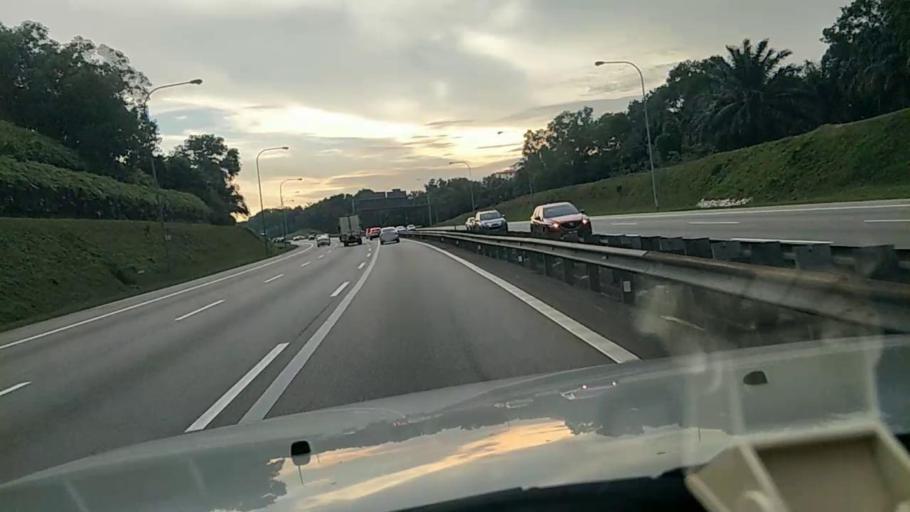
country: MY
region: Selangor
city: Shah Alam
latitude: 3.0951
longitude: 101.5379
